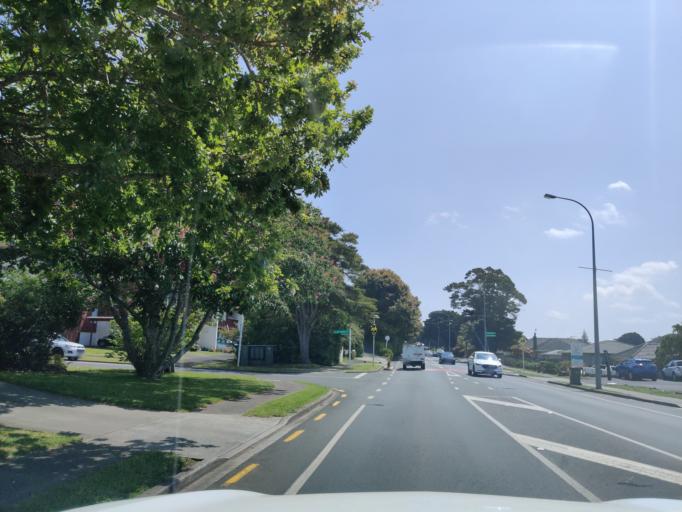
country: NZ
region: Auckland
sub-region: Auckland
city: Pukekohe East
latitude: -37.1974
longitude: 174.9164
